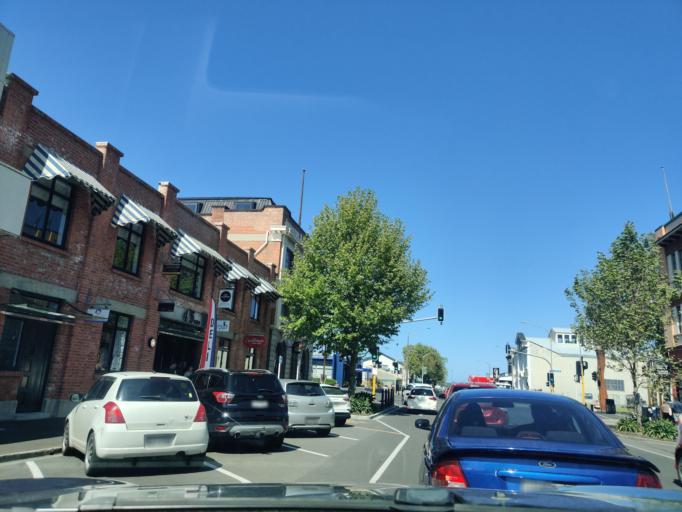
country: NZ
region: Manawatu-Wanganui
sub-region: Wanganui District
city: Wanganui
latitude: -39.9345
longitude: 175.0558
